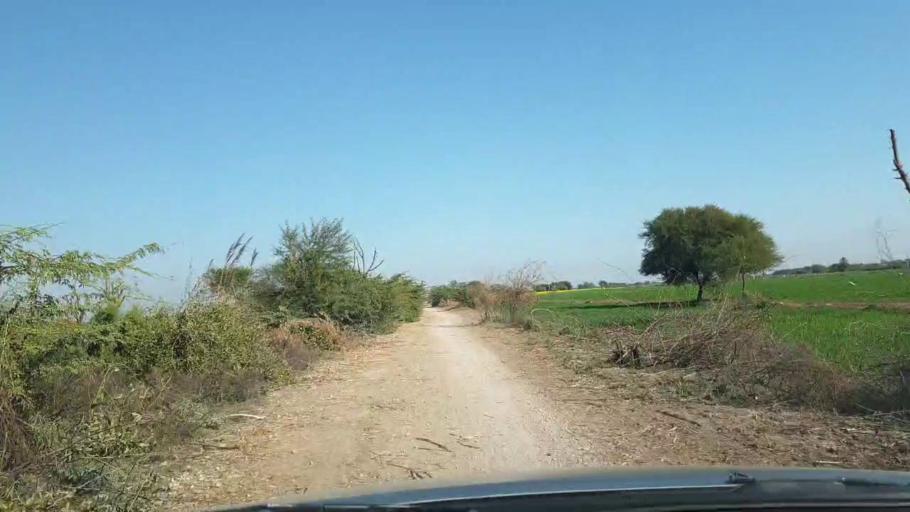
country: PK
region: Sindh
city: Jhol
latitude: 25.9158
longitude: 68.9664
